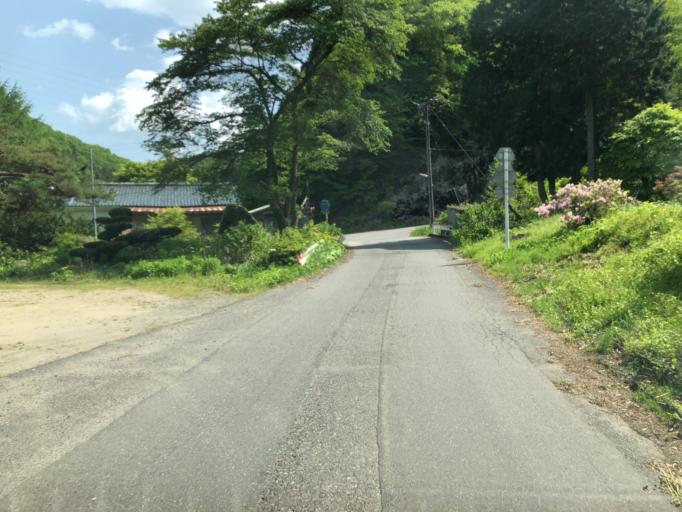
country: JP
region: Fukushima
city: Ishikawa
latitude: 37.0254
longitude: 140.5642
